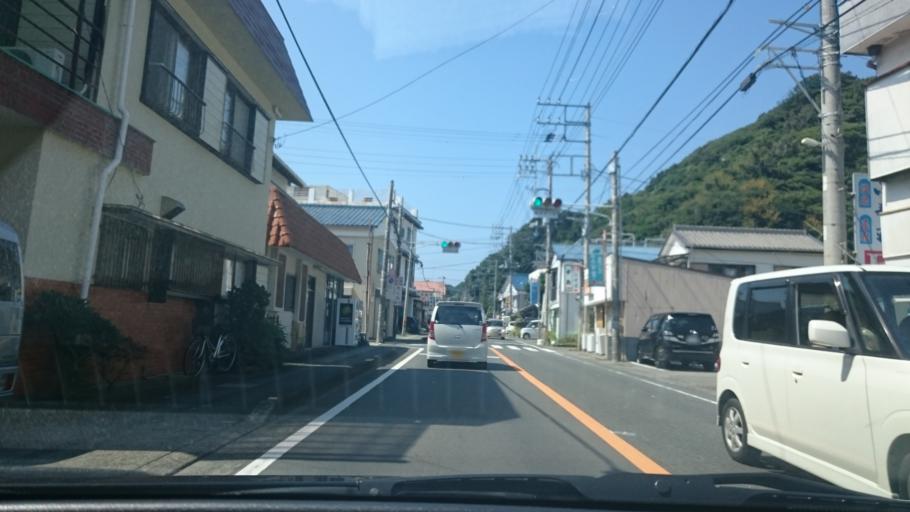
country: JP
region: Shizuoka
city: Heda
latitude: 34.7767
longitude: 138.7699
